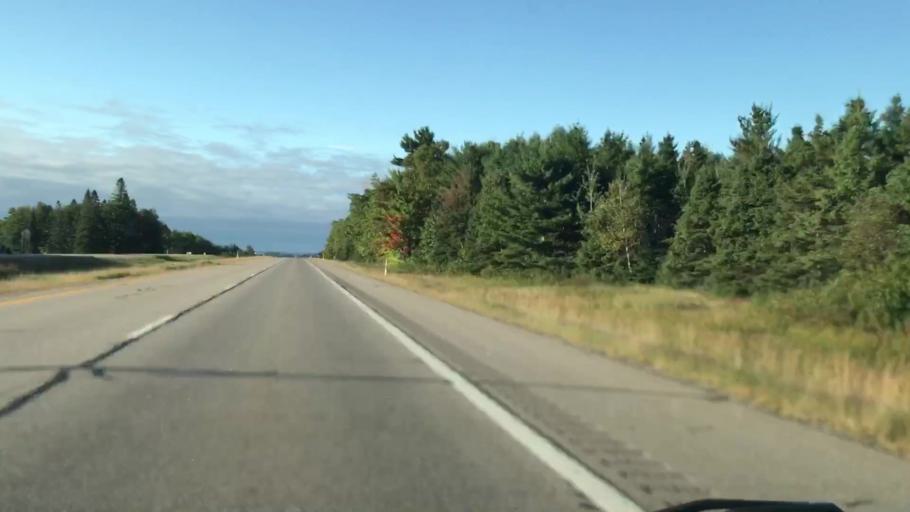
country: US
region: Michigan
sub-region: Chippewa County
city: Sault Ste. Marie
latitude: 46.4276
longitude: -84.3921
